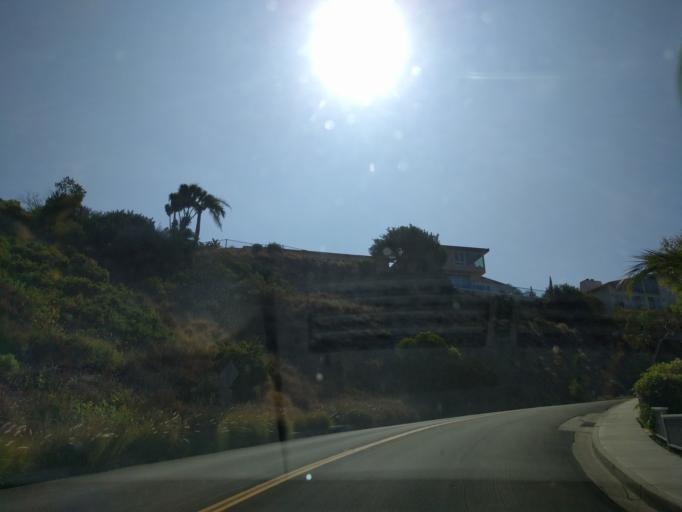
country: US
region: California
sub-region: Orange County
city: Laguna Beach
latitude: 33.5227
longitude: -117.7558
